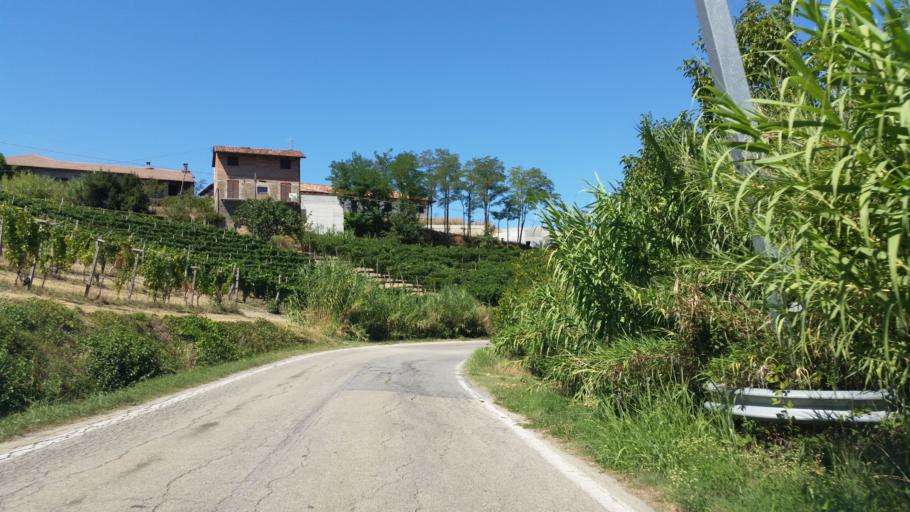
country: IT
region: Piedmont
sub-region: Provincia di Cuneo
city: Neive-Borgonovo
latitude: 44.7215
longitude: 8.1092
